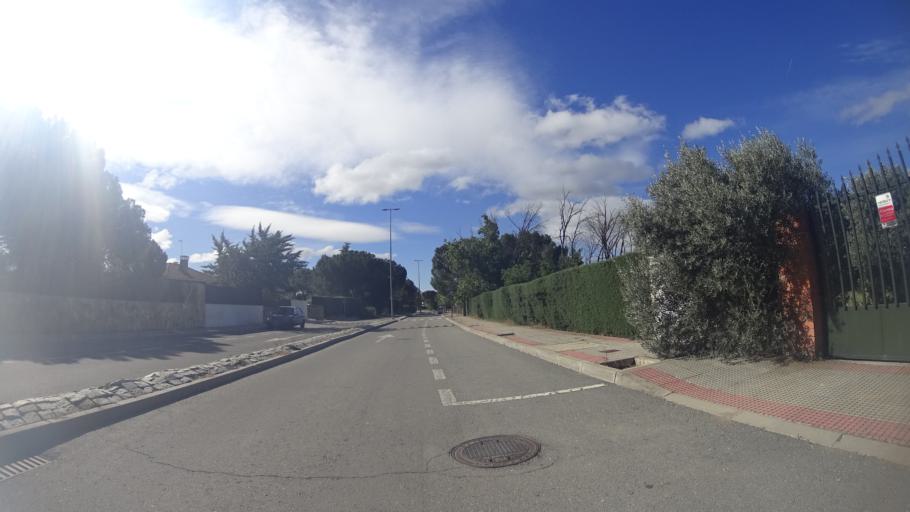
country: ES
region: Madrid
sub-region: Provincia de Madrid
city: Villanueva del Pardillo
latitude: 40.4904
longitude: -3.9405
